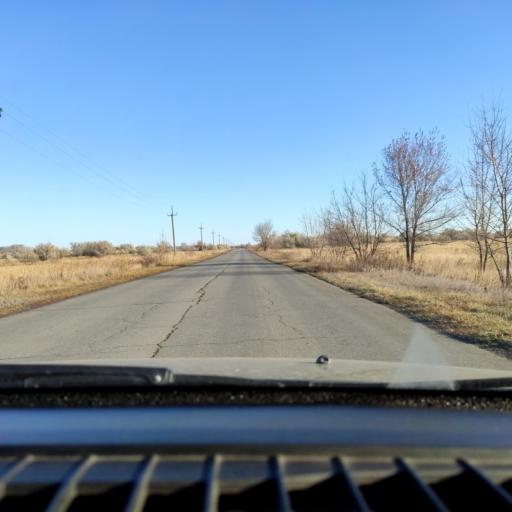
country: RU
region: Samara
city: Tol'yatti
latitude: 53.6508
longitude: 49.3231
